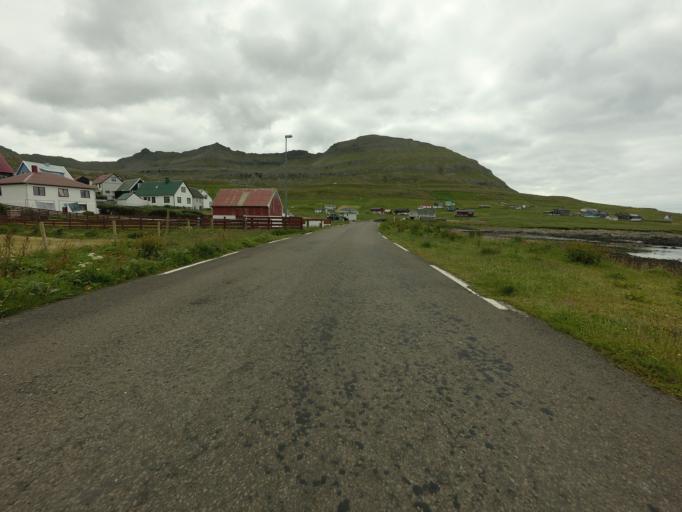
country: FO
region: Suduroy
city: Tvoroyri
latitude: 61.5244
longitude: -6.8793
